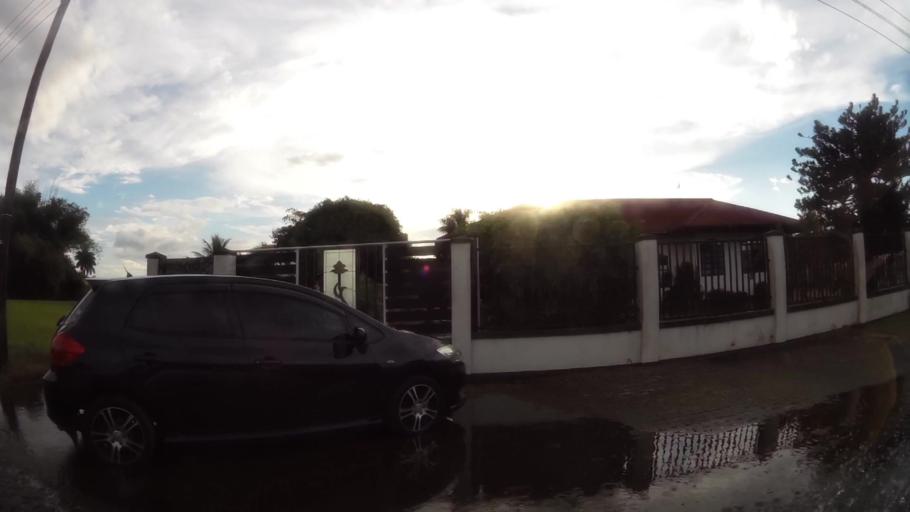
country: SR
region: Paramaribo
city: Paramaribo
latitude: 5.8375
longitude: -55.1882
